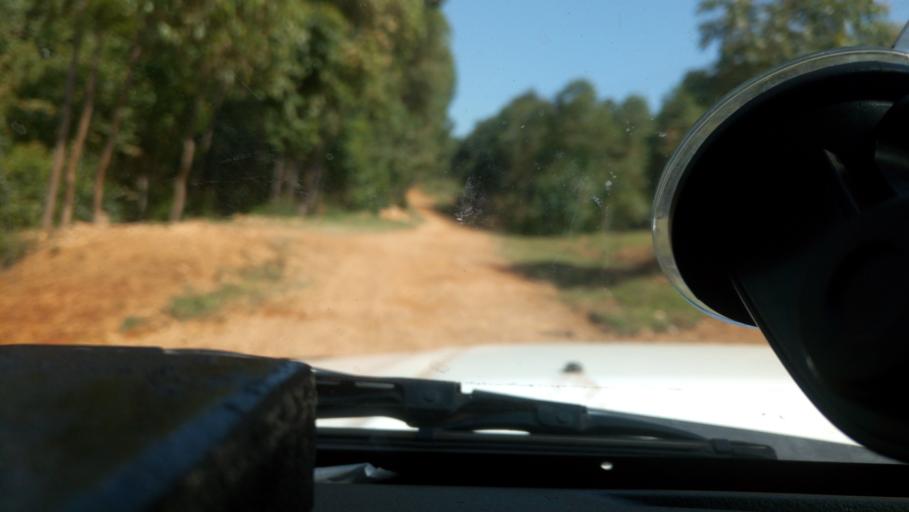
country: KE
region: Kisii
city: Ogembo
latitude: -0.7286
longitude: 34.7075
